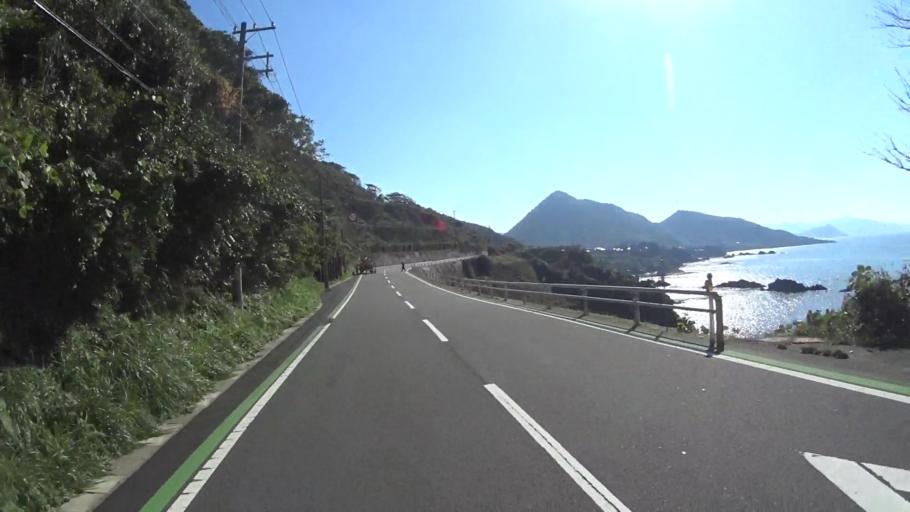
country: JP
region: Kyoto
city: Miyazu
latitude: 35.7289
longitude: 135.0872
